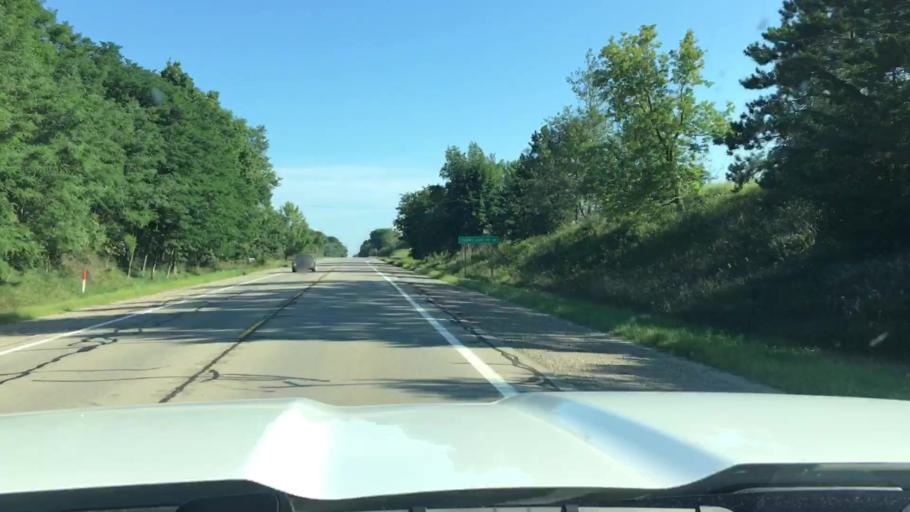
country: US
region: Michigan
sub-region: Ionia County
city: Ionia
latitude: 43.1325
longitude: -85.0747
